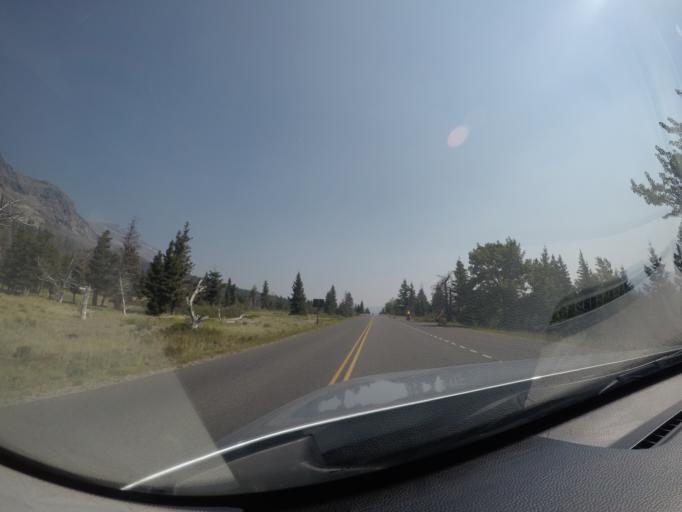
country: US
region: Montana
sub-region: Glacier County
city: Browning
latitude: 48.6927
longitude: -113.5213
